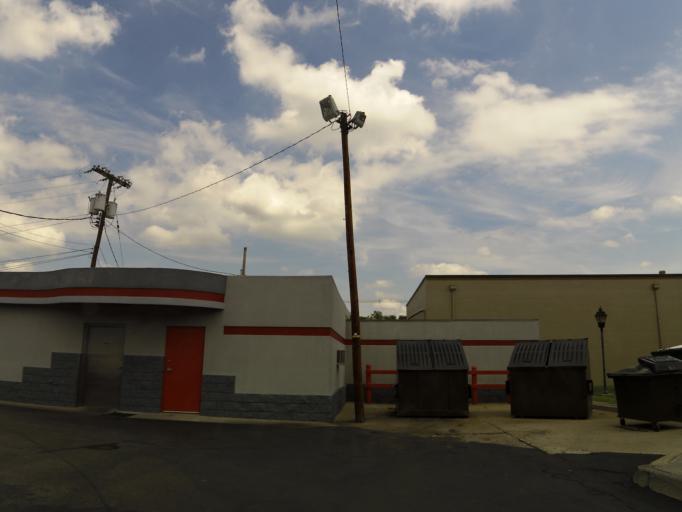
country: US
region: Tennessee
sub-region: Sullivan County
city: Kingsport
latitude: 36.5498
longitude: -82.5617
